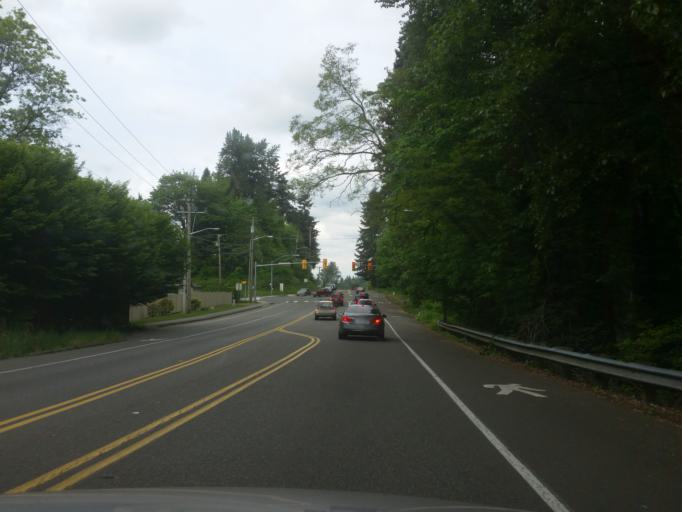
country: US
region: Washington
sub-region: King County
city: Inglewood-Finn Hill
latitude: 47.7297
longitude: -122.2078
